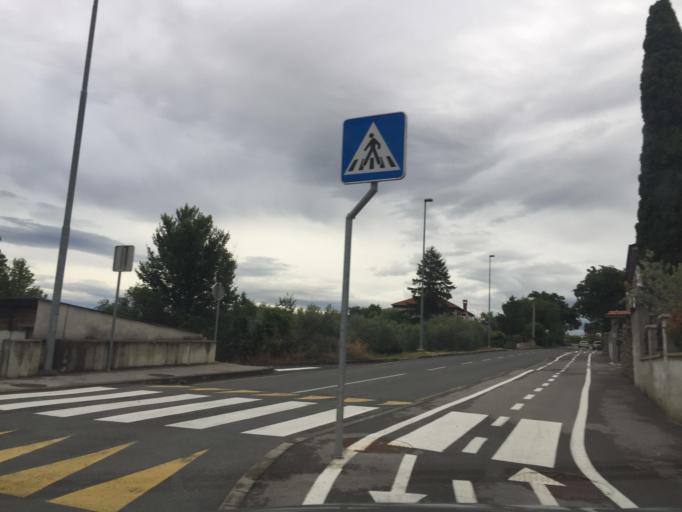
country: SI
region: Koper-Capodistria
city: Hrvatini
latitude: 45.5814
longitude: 13.7644
